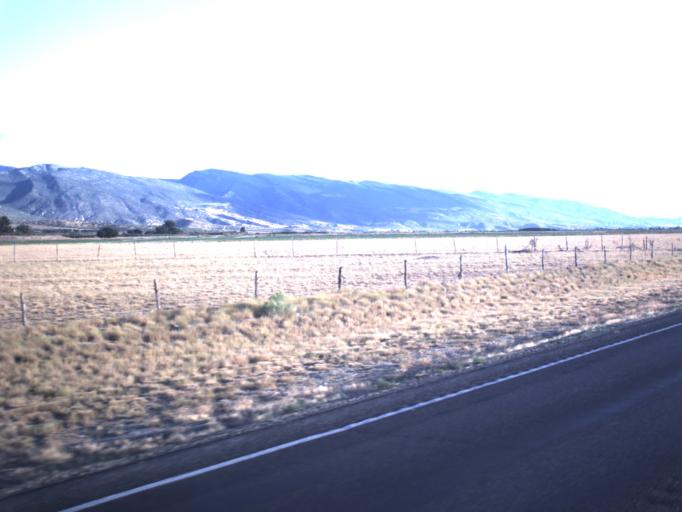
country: US
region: Utah
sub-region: Sanpete County
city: Ephraim
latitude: 39.4015
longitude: -111.5696
